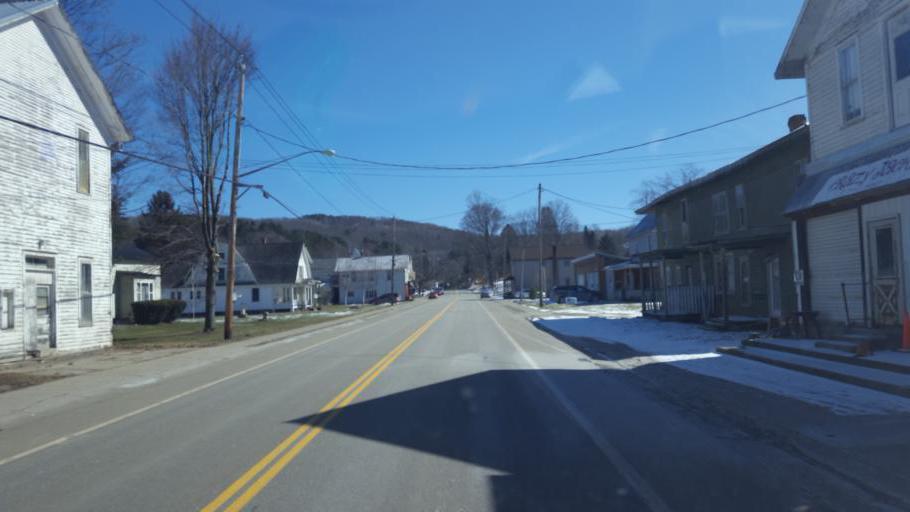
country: US
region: New York
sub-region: Allegany County
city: Andover
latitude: 42.0377
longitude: -77.7662
